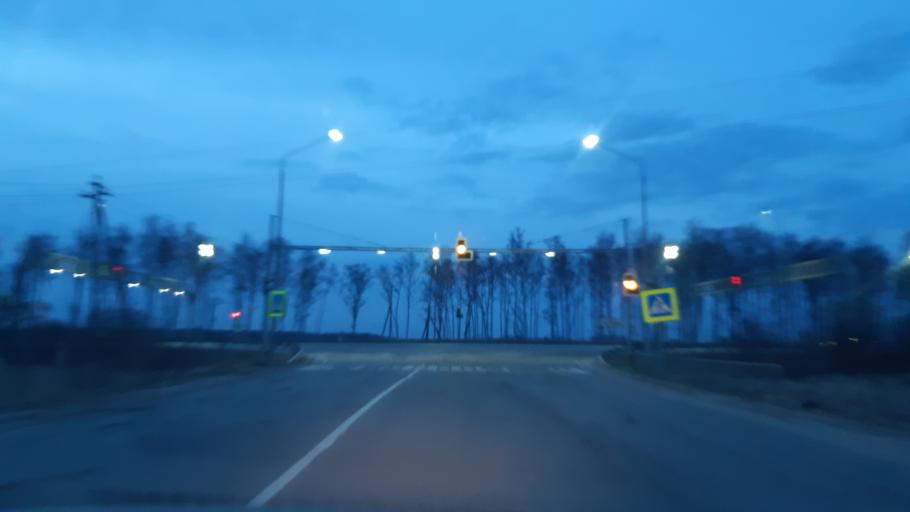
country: RU
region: Vladimir
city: Luknovo
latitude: 56.2377
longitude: 42.0341
